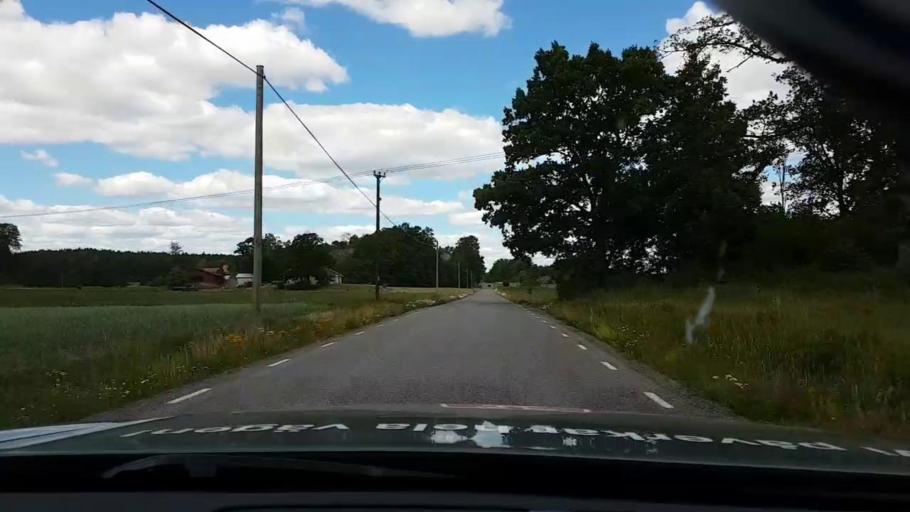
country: SE
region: Kalmar
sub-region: Vasterviks Kommun
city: Forserum
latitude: 57.9905
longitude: 16.6039
